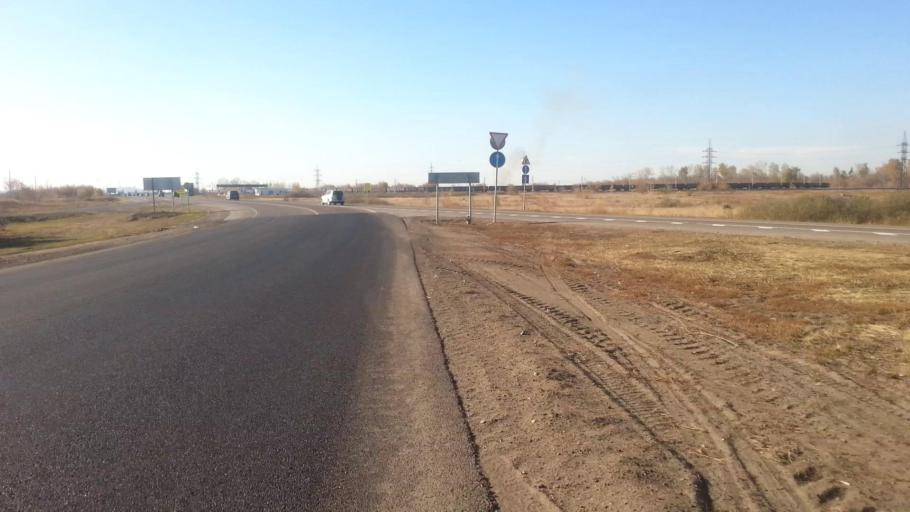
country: RU
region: Altai Krai
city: Novoaltaysk
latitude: 53.3727
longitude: 83.9522
